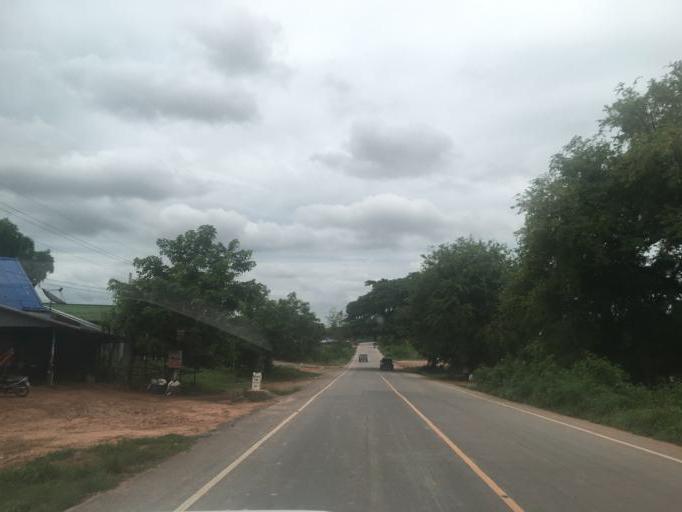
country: TH
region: Changwat Udon Thani
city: Nong Saeng
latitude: 17.2827
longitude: 102.7073
